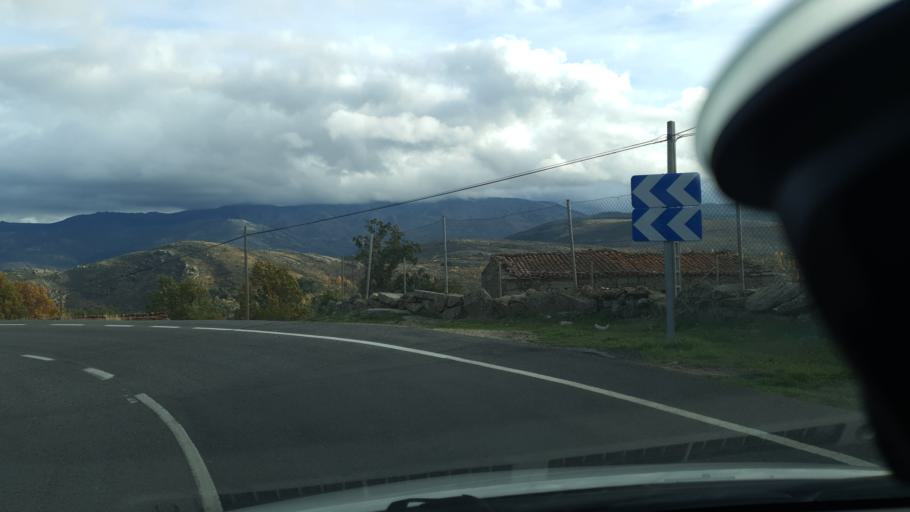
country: ES
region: Castille and Leon
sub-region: Provincia de Avila
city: Navalosa
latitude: 40.3978
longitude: -4.9306
